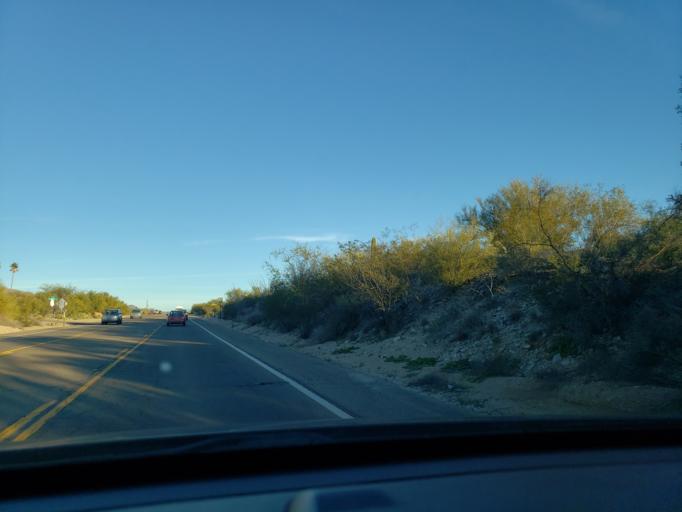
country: US
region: Arizona
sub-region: Pima County
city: Catalina Foothills
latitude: 32.3226
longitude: -110.9486
